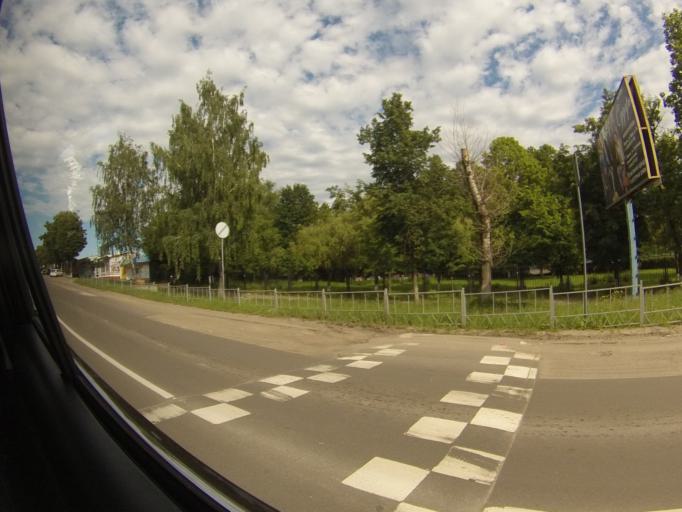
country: RU
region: Orjol
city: Mtsensk
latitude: 53.2886
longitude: 36.5930
